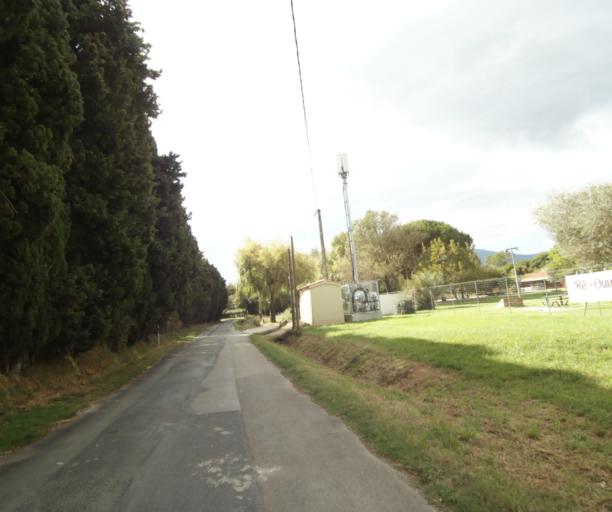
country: FR
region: Languedoc-Roussillon
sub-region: Departement des Pyrenees-Orientales
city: Argelers
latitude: 42.5716
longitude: 3.0263
